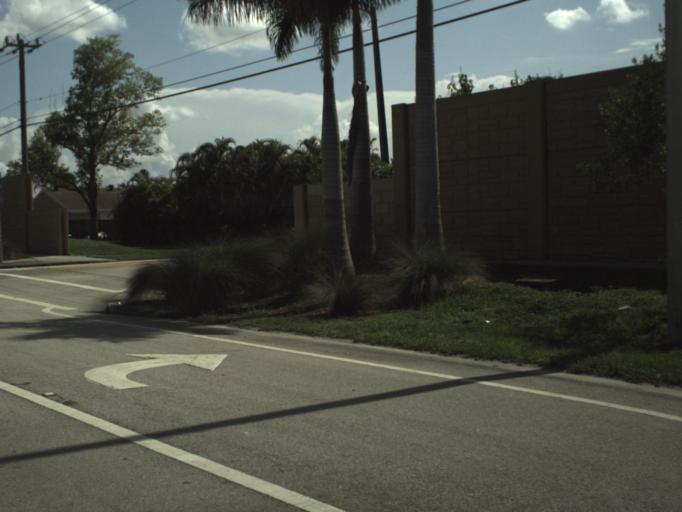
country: US
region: Florida
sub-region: Palm Beach County
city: Royal Palm Beach
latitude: 26.6983
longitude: -80.2015
